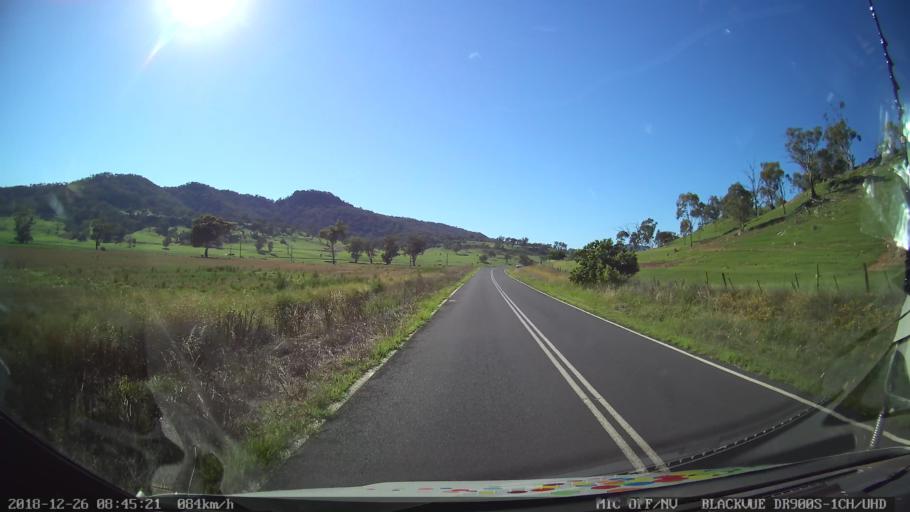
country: AU
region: New South Wales
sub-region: Mid-Western Regional
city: Kandos
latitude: -32.5242
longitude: 150.0861
